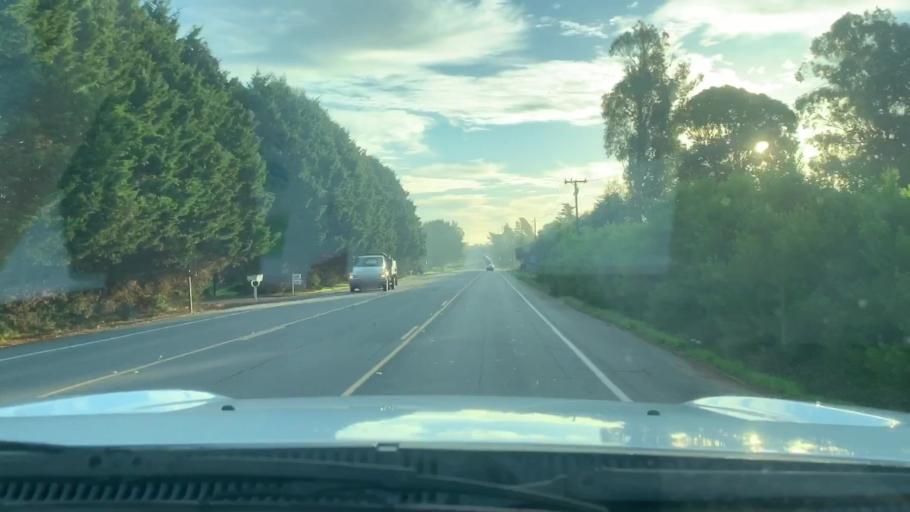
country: US
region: California
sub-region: San Luis Obispo County
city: Los Osos
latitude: 35.3054
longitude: -120.8092
